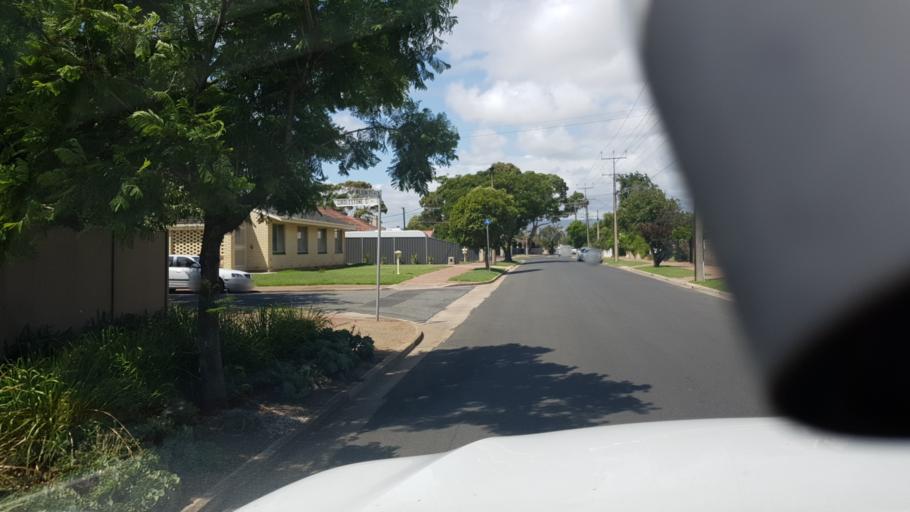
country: AU
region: South Australia
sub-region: Holdfast Bay
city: Glenelg East
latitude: -34.9853
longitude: 138.5276
